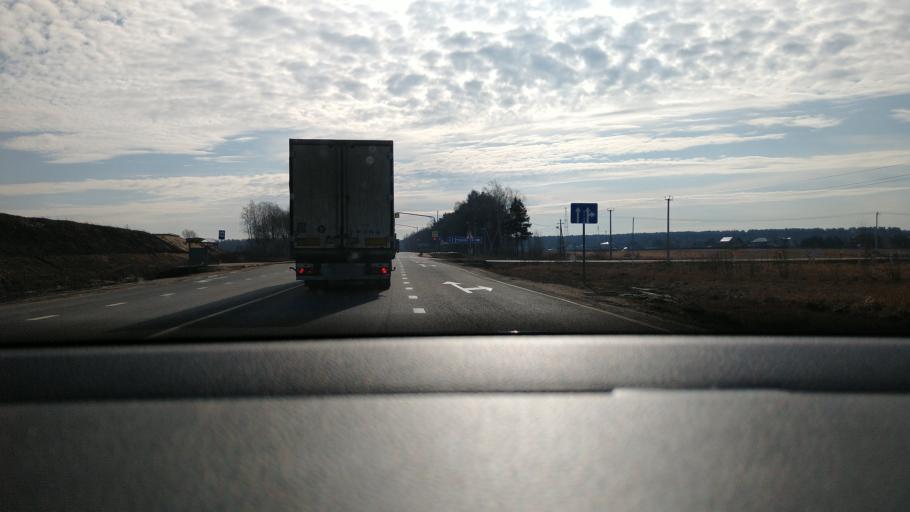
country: RU
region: Moskovskaya
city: L'vovskiy
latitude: 55.3492
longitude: 37.4494
